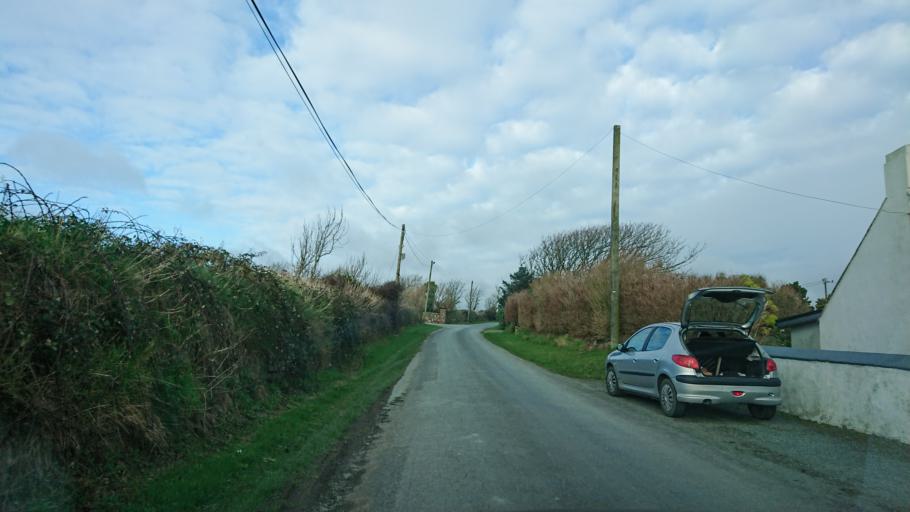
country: IE
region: Munster
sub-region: Waterford
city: Portlaw
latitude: 52.1399
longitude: -7.3058
